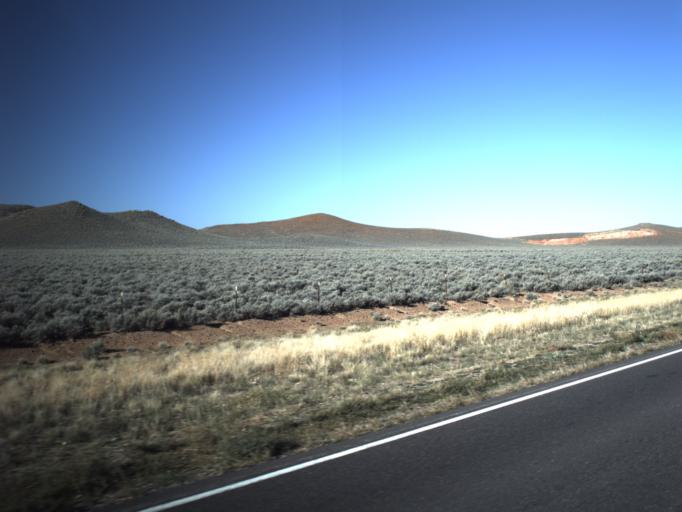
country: US
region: Utah
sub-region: Washington County
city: Enterprise
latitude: 37.7359
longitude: -113.7297
